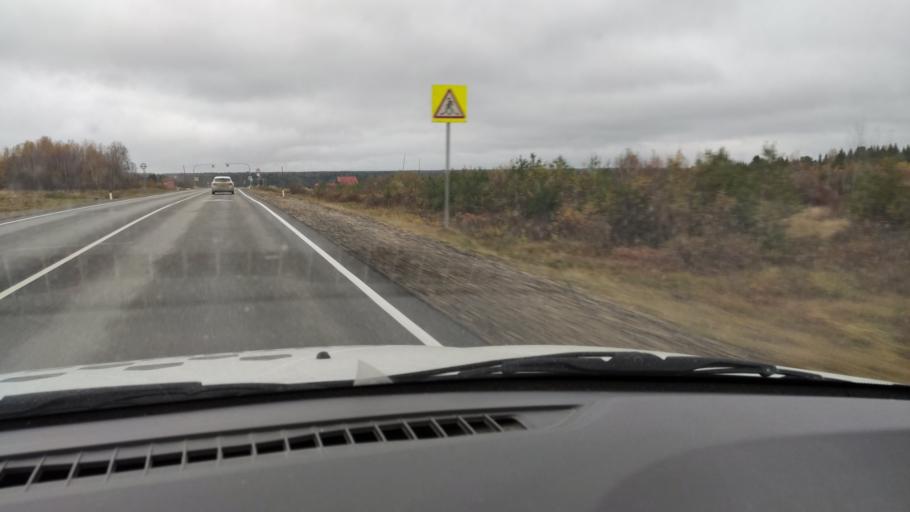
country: RU
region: Kirov
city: Chernaya Kholunitsa
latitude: 58.8582
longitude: 51.7117
